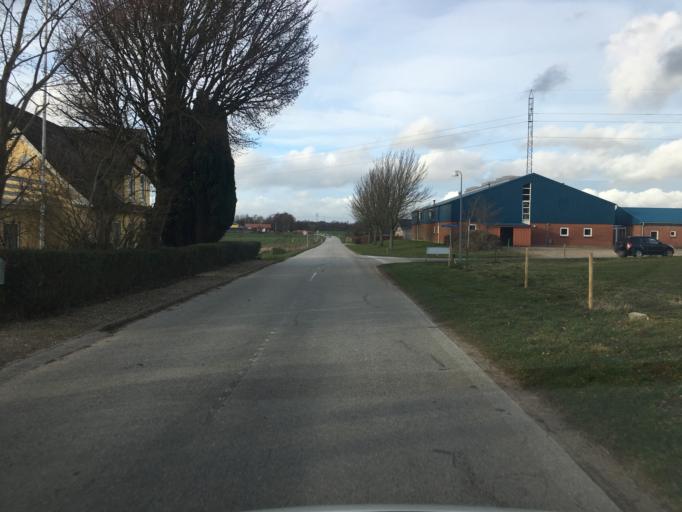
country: DK
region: South Denmark
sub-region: Sonderborg Kommune
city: Grasten
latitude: 54.9771
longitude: 9.5184
